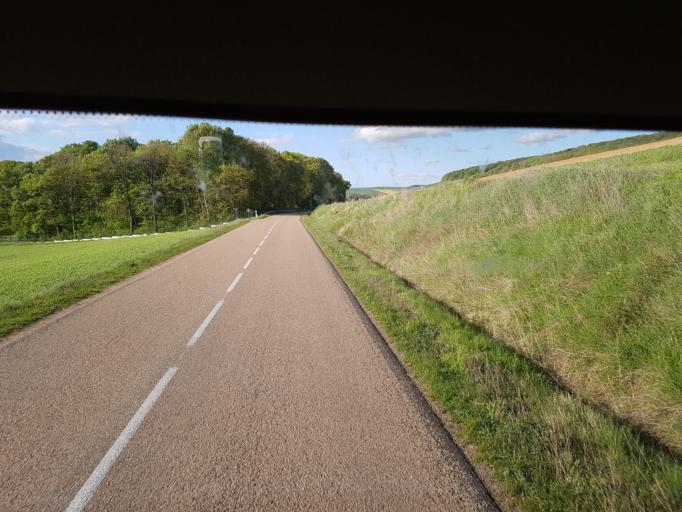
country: FR
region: Champagne-Ardenne
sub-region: Departement de l'Aube
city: Aix-en-Othe
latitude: 48.1788
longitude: 3.6248
